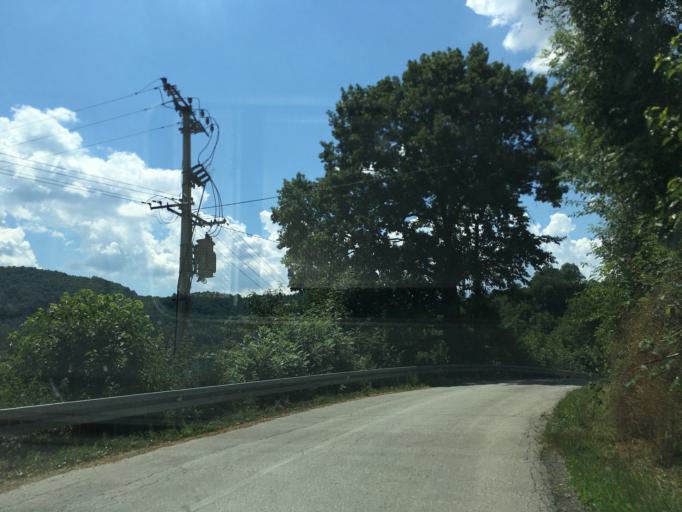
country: RS
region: Central Serbia
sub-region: Kolubarski Okrug
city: Ljig
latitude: 44.2331
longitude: 20.3523
